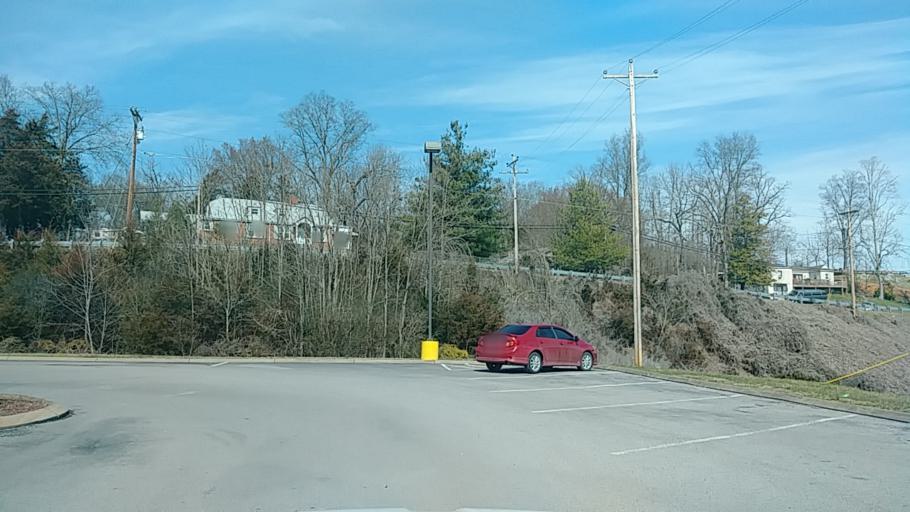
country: US
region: Tennessee
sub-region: Claiborne County
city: Tazewell
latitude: 36.4485
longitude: -83.5763
